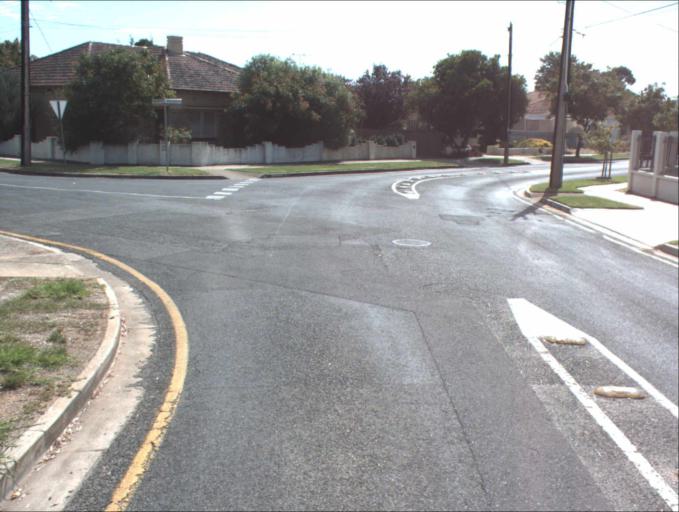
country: AU
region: South Australia
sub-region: Port Adelaide Enfield
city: Klemzig
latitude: -34.8788
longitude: 138.6220
